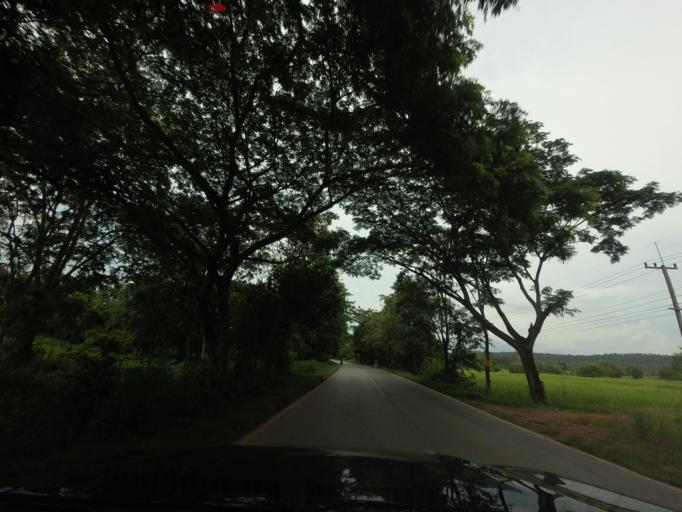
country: TH
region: Changwat Nong Bua Lamphu
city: Suwannakhuha
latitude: 17.4791
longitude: 102.3619
